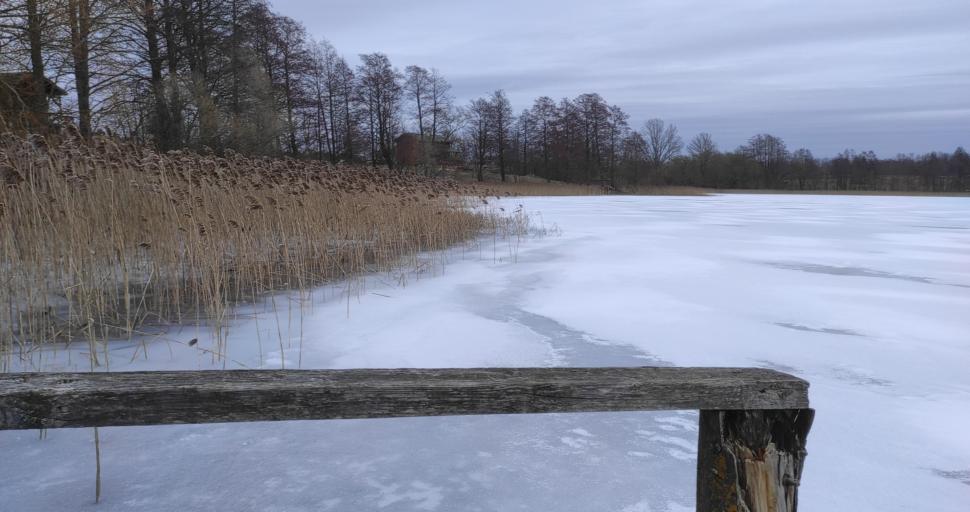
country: LV
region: Tukuma Rajons
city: Tukums
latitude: 57.0981
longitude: 23.0879
